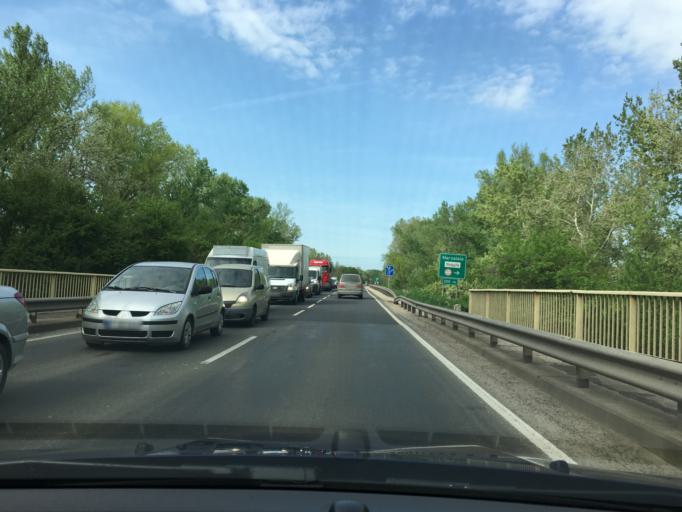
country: HU
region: Csongrad
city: Algyo
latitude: 46.3537
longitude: 20.2069
